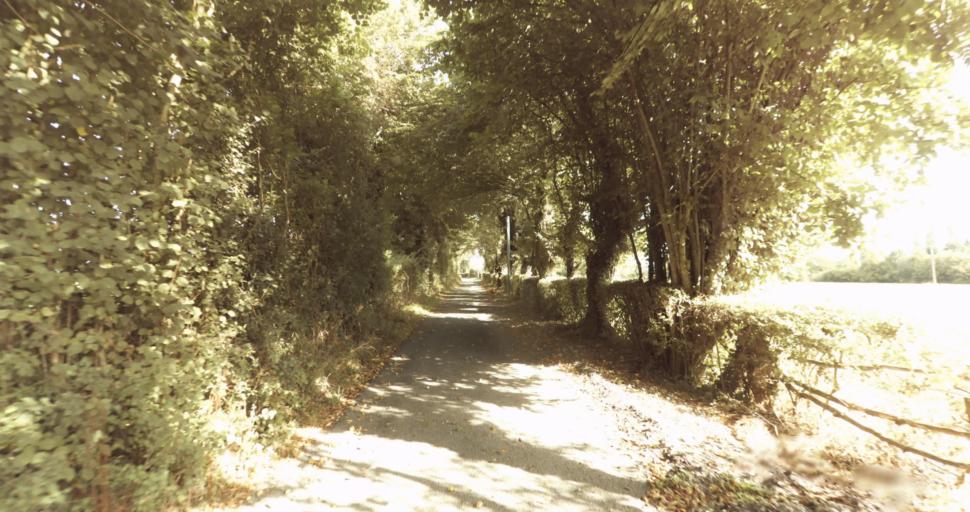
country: FR
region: Lower Normandy
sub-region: Departement de l'Orne
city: Gace
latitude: 48.8229
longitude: 0.2128
